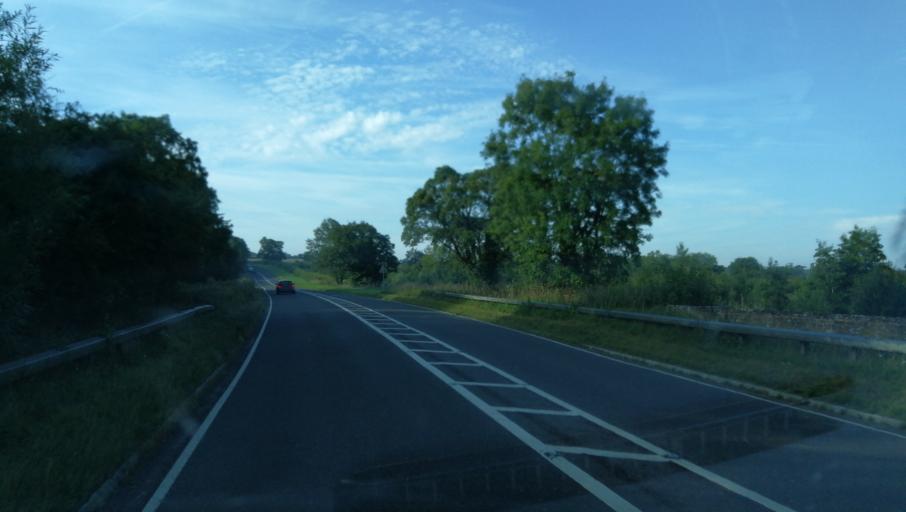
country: GB
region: England
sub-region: Oxfordshire
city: Deddington
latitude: 51.9688
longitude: -1.3201
